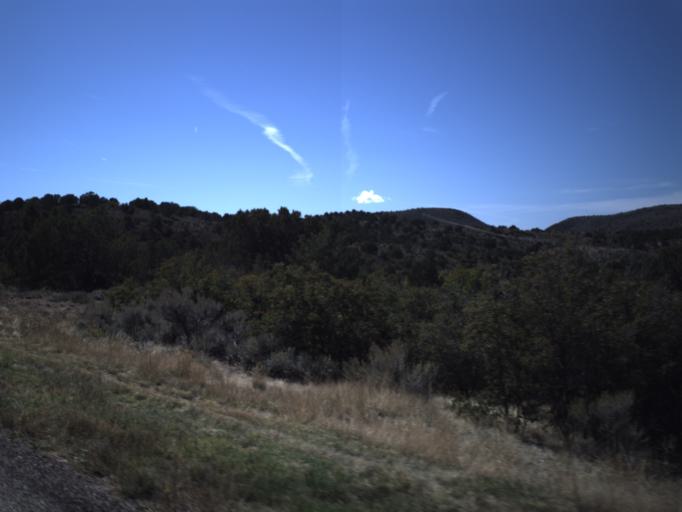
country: US
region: Utah
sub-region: Washington County
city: Enterprise
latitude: 37.4773
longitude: -113.6280
